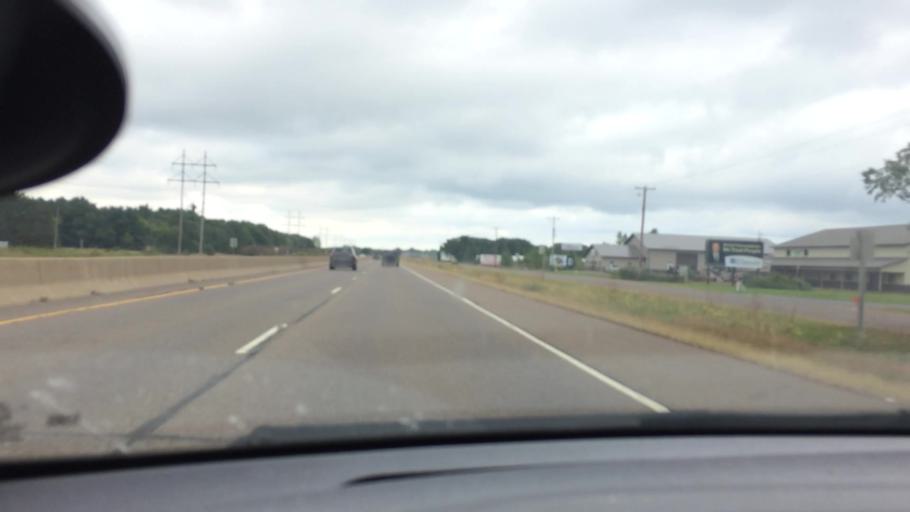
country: US
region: Wisconsin
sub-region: Chippewa County
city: Chippewa Falls
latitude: 44.9055
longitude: -91.4086
